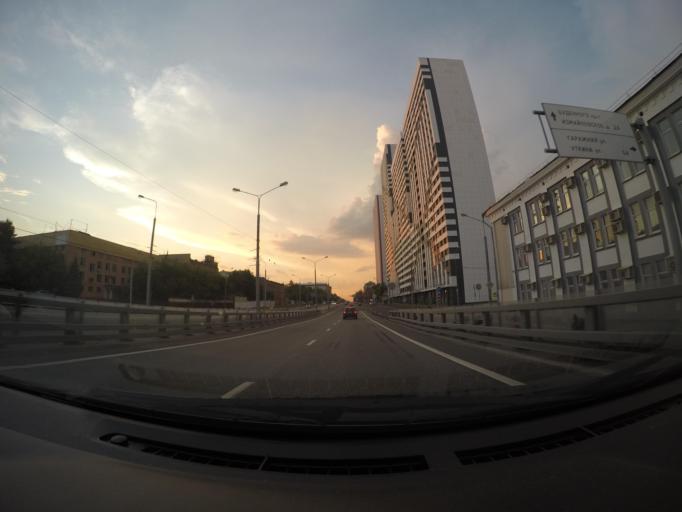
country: RU
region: Moscow
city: Ryazanskiy
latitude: 55.7580
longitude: 37.7395
